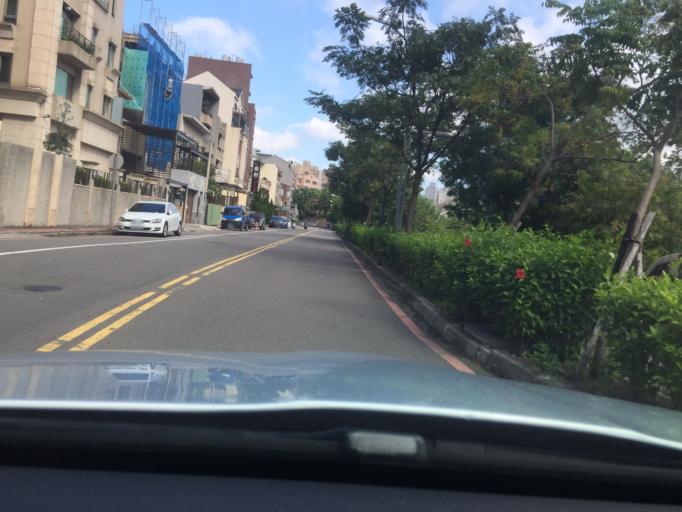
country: TW
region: Taiwan
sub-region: Hsinchu
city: Zhubei
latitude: 24.8292
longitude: 121.0140
